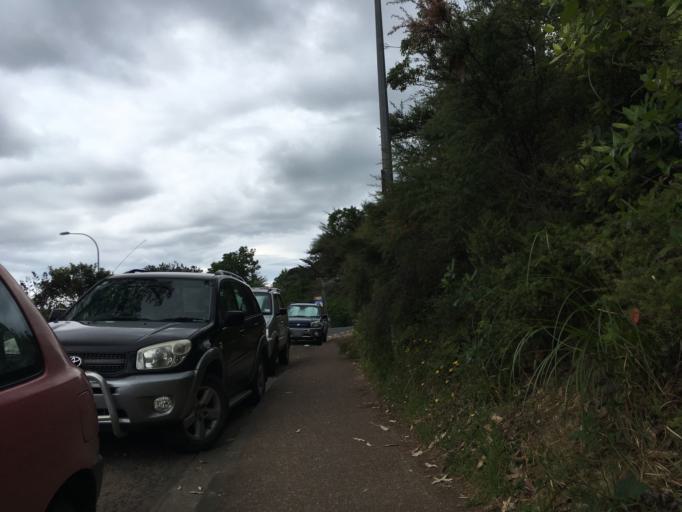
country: NZ
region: Auckland
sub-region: Auckland
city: Pakuranga
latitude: -36.7815
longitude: 174.9960
